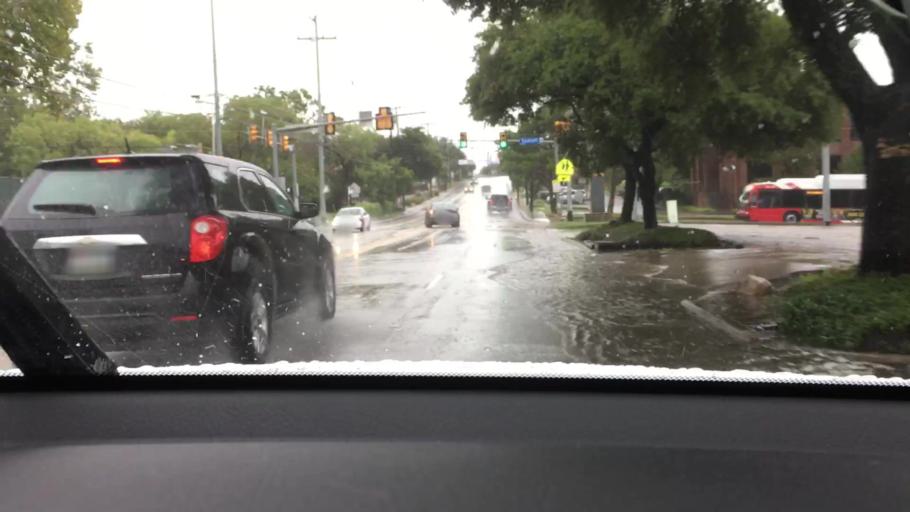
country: US
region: Texas
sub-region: Bexar County
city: Alamo Heights
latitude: 29.5077
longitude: -98.4663
